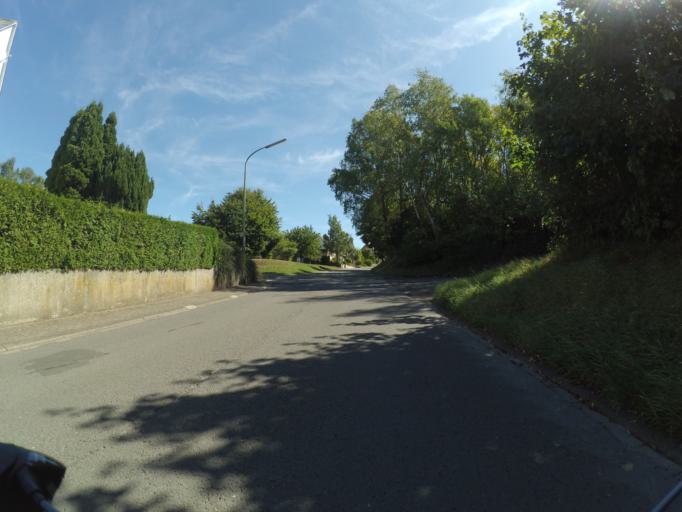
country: DE
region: Rheinland-Pfalz
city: Morbach
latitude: 49.7897
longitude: 7.0977
